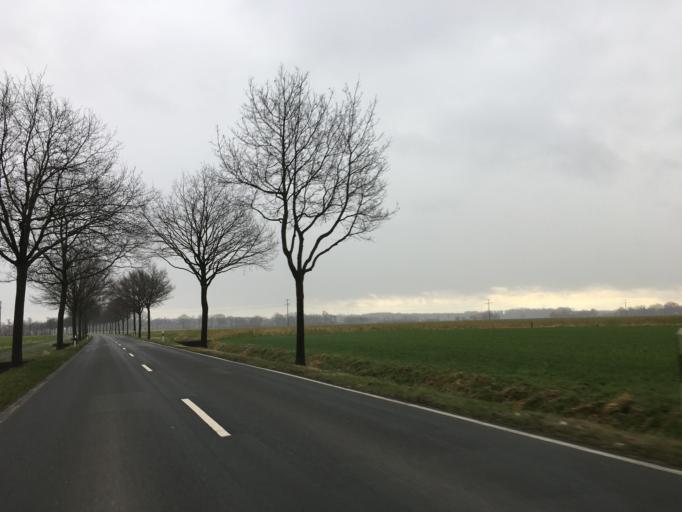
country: DE
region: North Rhine-Westphalia
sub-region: Regierungsbezirk Munster
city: Senden
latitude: 51.8549
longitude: 7.4329
